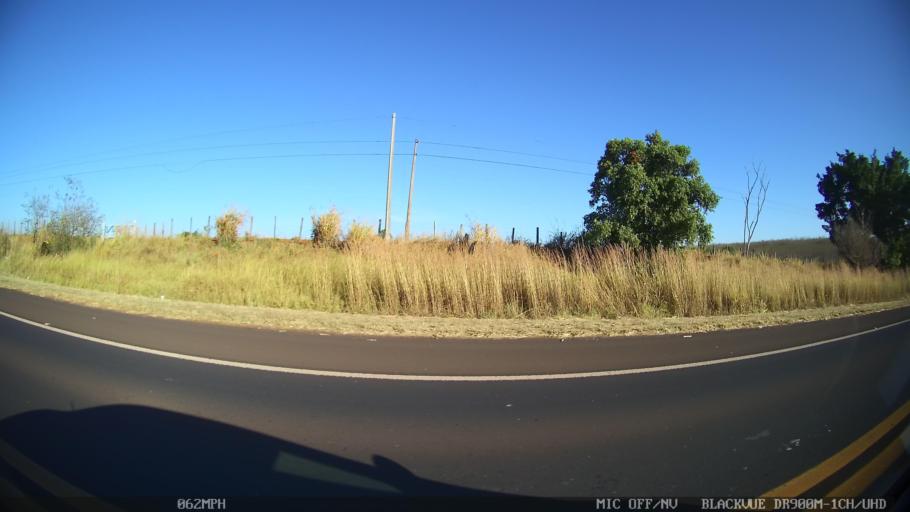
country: BR
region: Sao Paulo
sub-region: Olimpia
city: Olimpia
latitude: -20.7117
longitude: -48.9793
